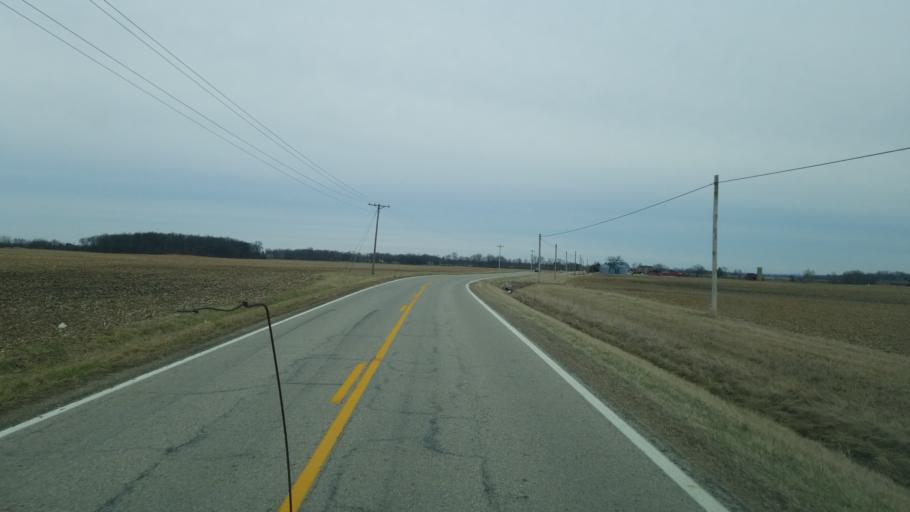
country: US
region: Ohio
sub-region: Pickaway County
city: Williamsport
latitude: 39.5636
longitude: -83.0811
